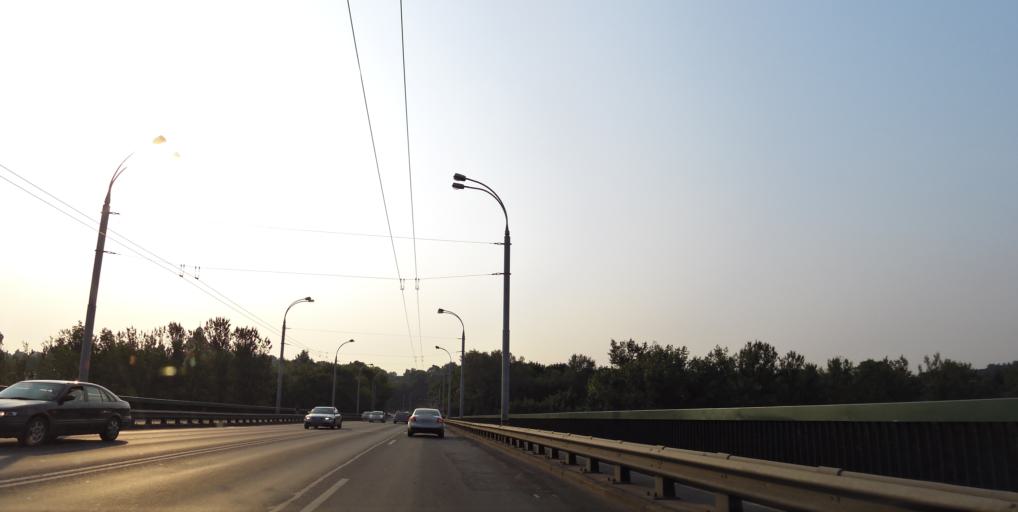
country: LT
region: Vilnius County
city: Rasos
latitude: 54.6949
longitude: 25.3013
